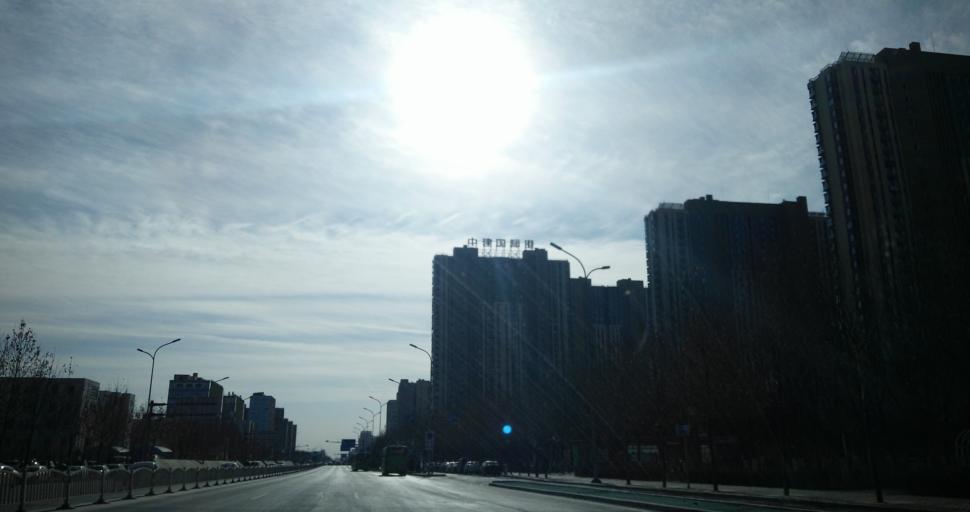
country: CN
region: Beijing
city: Daxing
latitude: 39.7561
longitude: 116.3260
